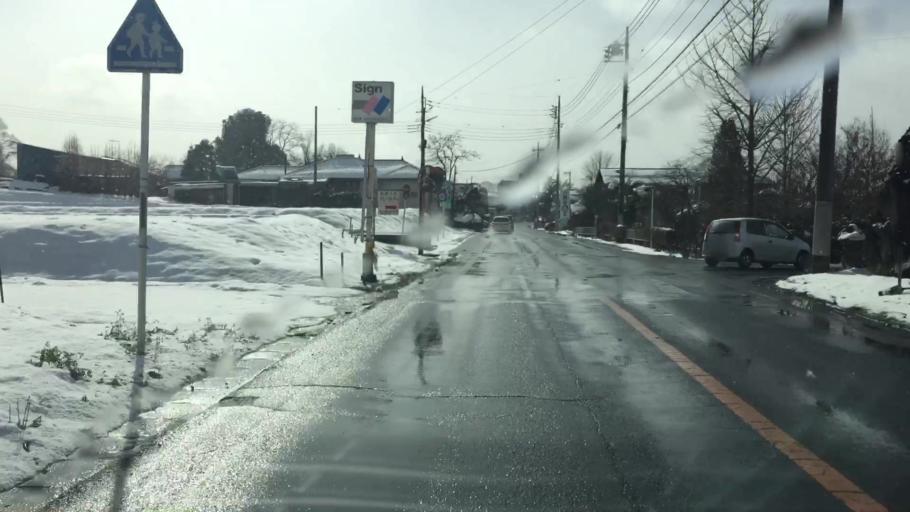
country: JP
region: Gunma
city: Numata
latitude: 36.6714
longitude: 139.0628
